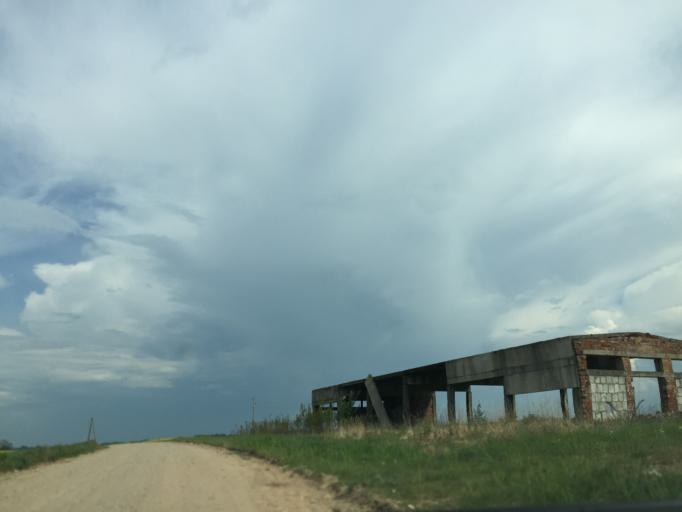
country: LV
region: Livani
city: Livani
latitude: 56.5779
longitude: 26.1764
